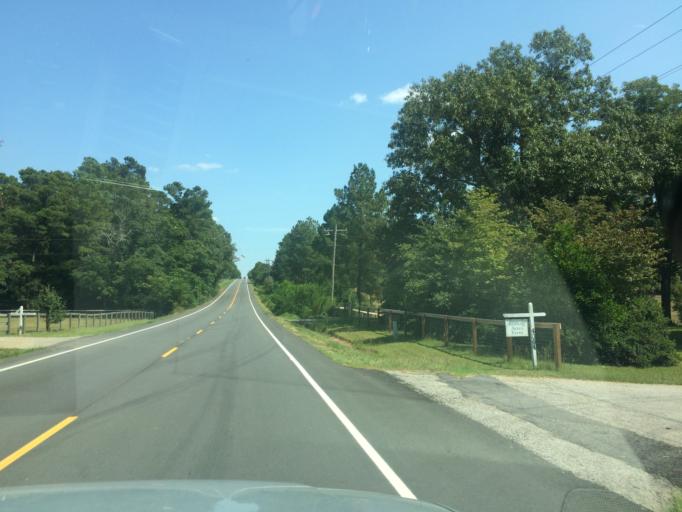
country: US
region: South Carolina
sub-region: Aiken County
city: Aiken
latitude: 33.5727
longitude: -81.5599
